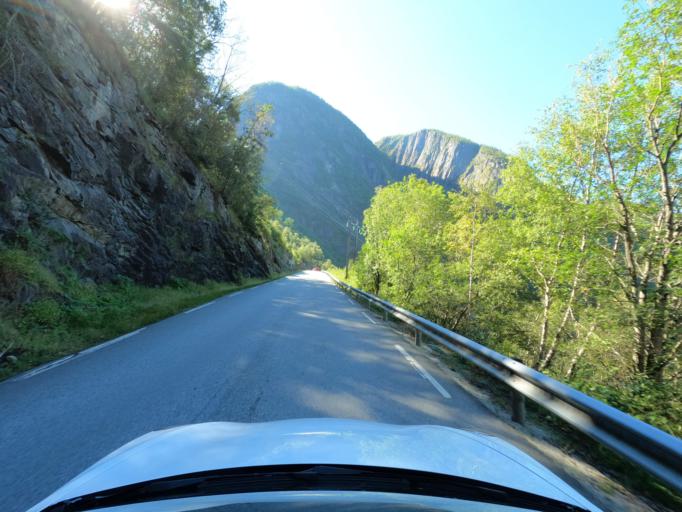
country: NO
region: Sogn og Fjordane
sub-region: Aurland
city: Aurlandsvangen
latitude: 60.8589
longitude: 7.3081
